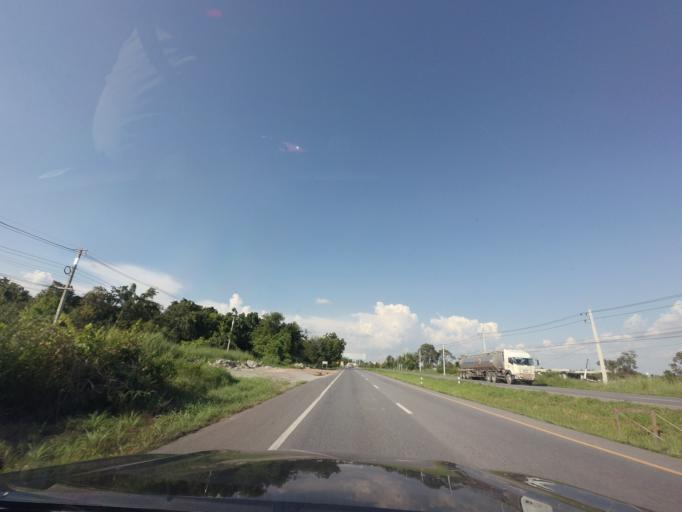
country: TH
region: Khon Kaen
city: Non Sila
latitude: 15.9570
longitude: 102.6870
